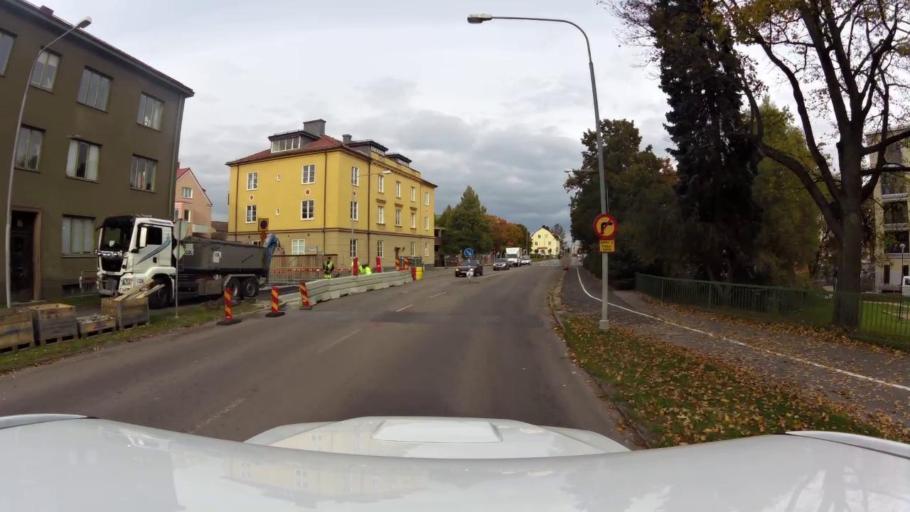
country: SE
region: OEstergoetland
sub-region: Linkopings Kommun
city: Linkoping
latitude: 58.4120
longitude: 15.6068
